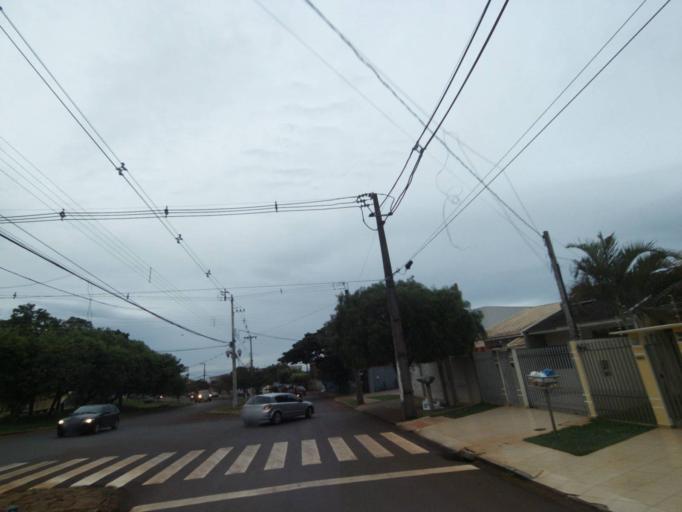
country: BR
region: Parana
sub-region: Campo Mourao
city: Campo Mourao
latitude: -24.0399
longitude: -52.3649
